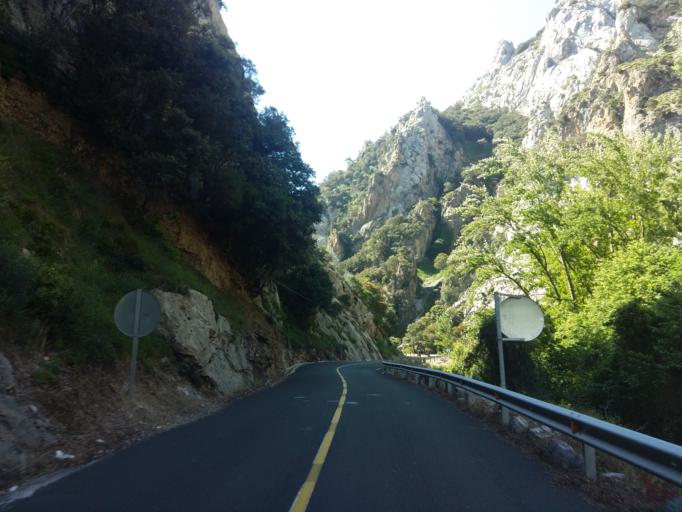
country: ES
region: Cantabria
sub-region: Provincia de Cantabria
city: Potes
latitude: 43.2051
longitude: -4.5937
